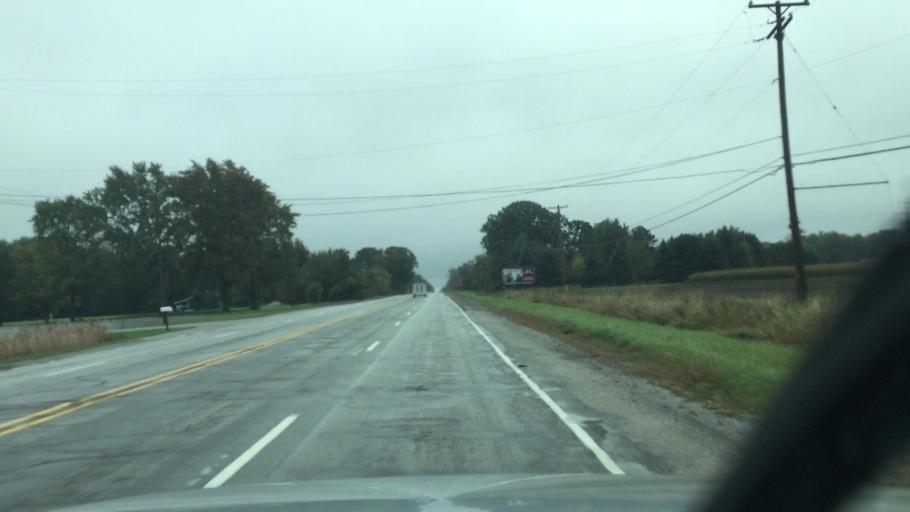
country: US
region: Michigan
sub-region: Saginaw County
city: Bridgeport
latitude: 43.3267
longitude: -83.8273
